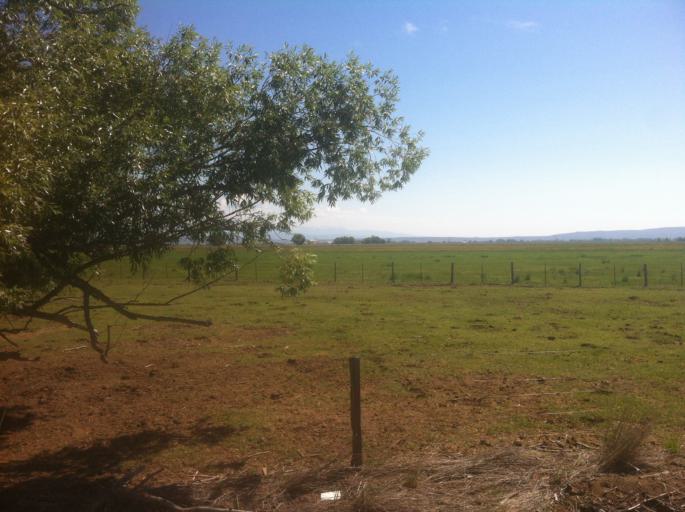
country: US
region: Oregon
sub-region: Baker County
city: Baker City
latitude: 44.8516
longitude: -117.8917
